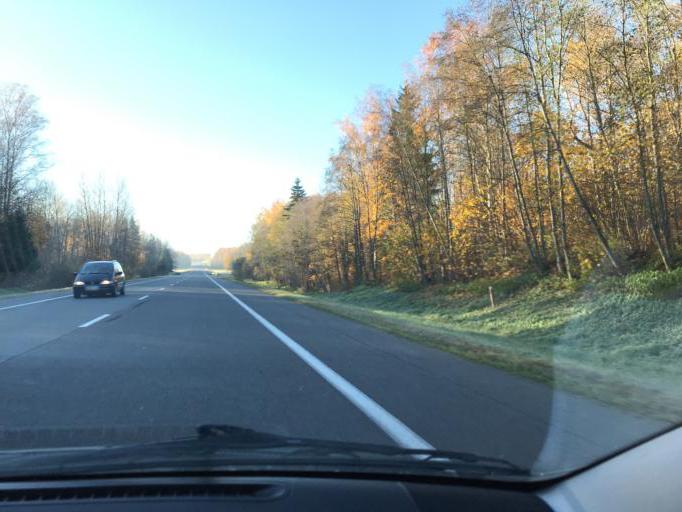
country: BY
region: Vitebsk
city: Vitebsk
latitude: 55.0638
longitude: 30.3101
